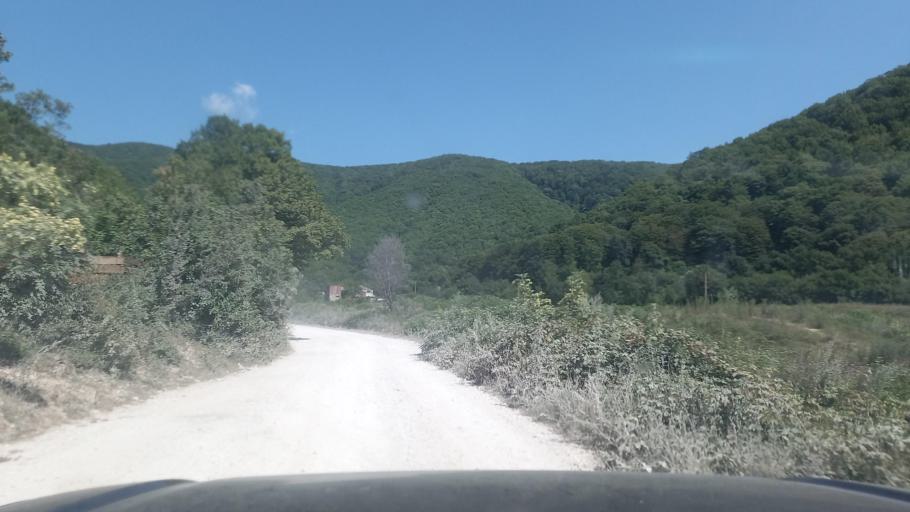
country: RU
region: Krasnodarskiy
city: Lermontovo
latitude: 44.3262
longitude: 38.7949
